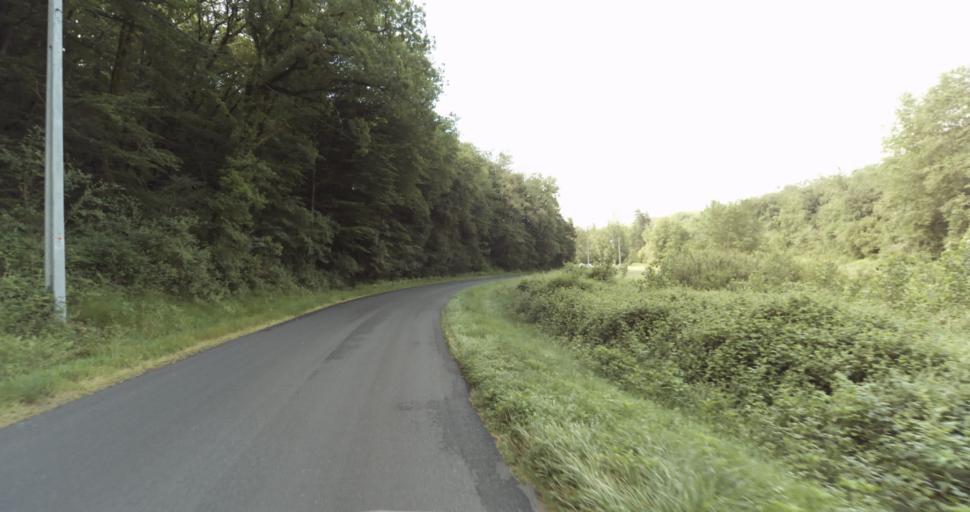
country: FR
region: Aquitaine
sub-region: Departement de la Dordogne
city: Lalinde
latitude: 44.8617
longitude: 0.7752
